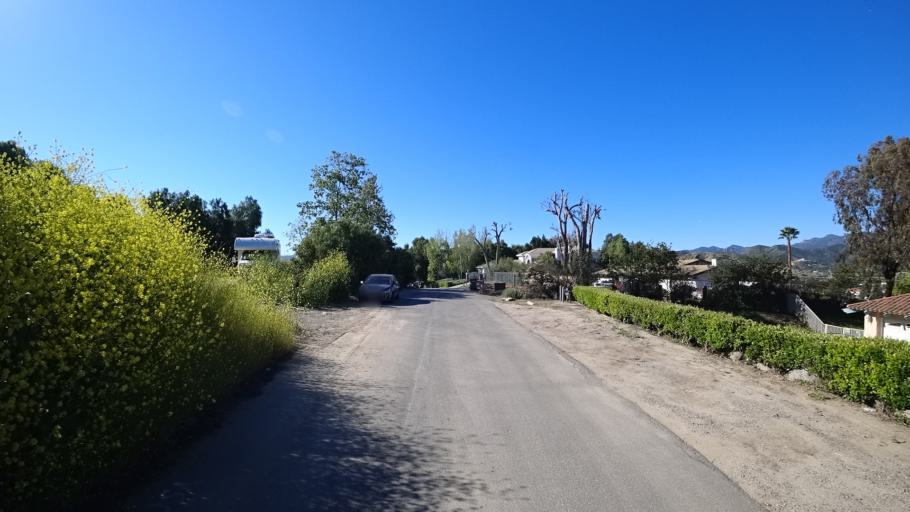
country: US
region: California
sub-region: Ventura County
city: Thousand Oaks
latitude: 34.1849
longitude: -118.8457
